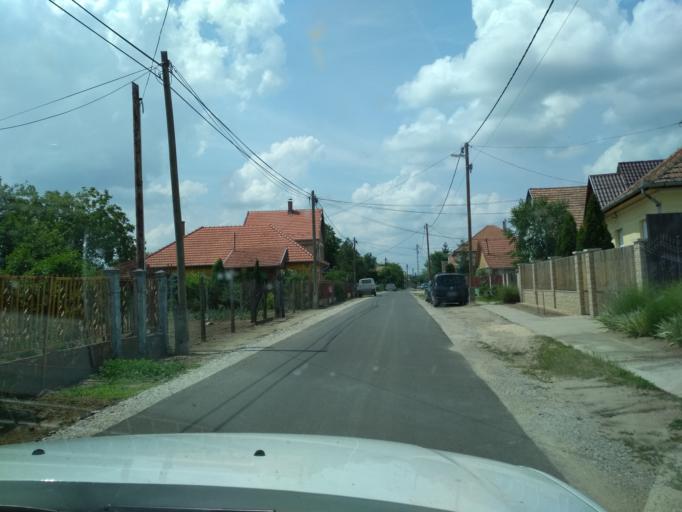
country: HU
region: Pest
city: Tapioszentmarton
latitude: 47.3450
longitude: 19.7428
